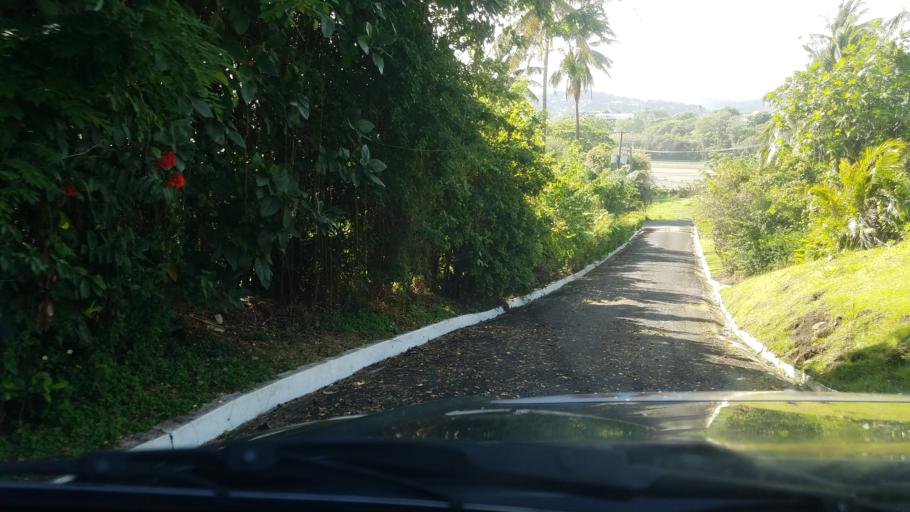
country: LC
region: Castries Quarter
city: Bisee
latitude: 14.0214
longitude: -60.9981
